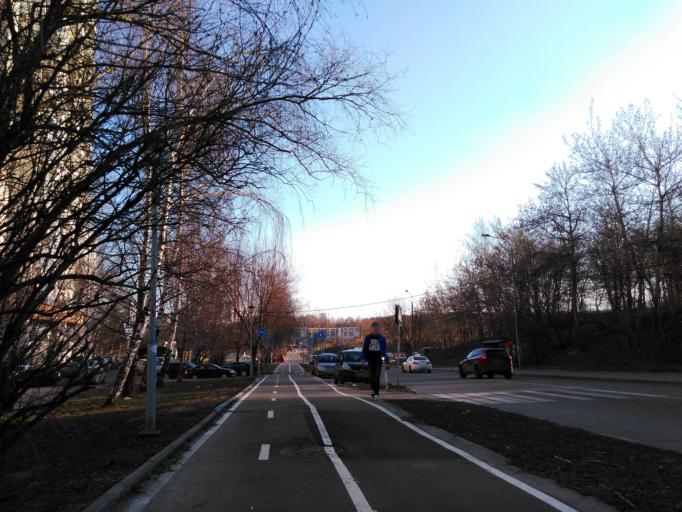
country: RU
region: Moscow
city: Kotlovka
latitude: 55.6345
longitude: 37.5886
